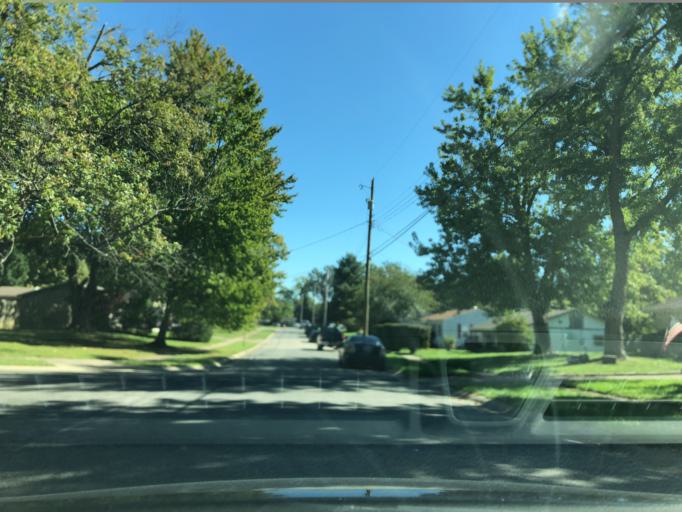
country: US
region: Ohio
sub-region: Hamilton County
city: Loveland
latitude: 39.2680
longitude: -84.2762
